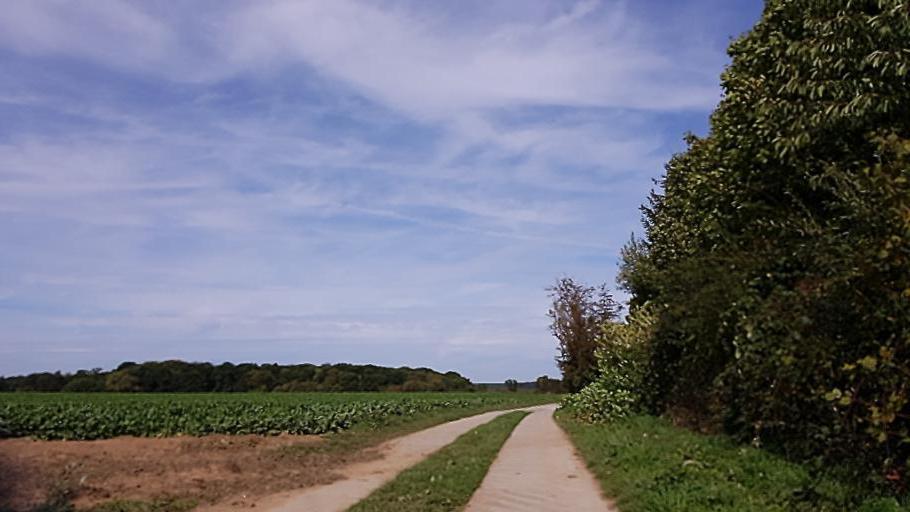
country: BE
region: Wallonia
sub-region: Province du Brabant Wallon
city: Grez-Doiceau
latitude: 50.7715
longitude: 4.6851
